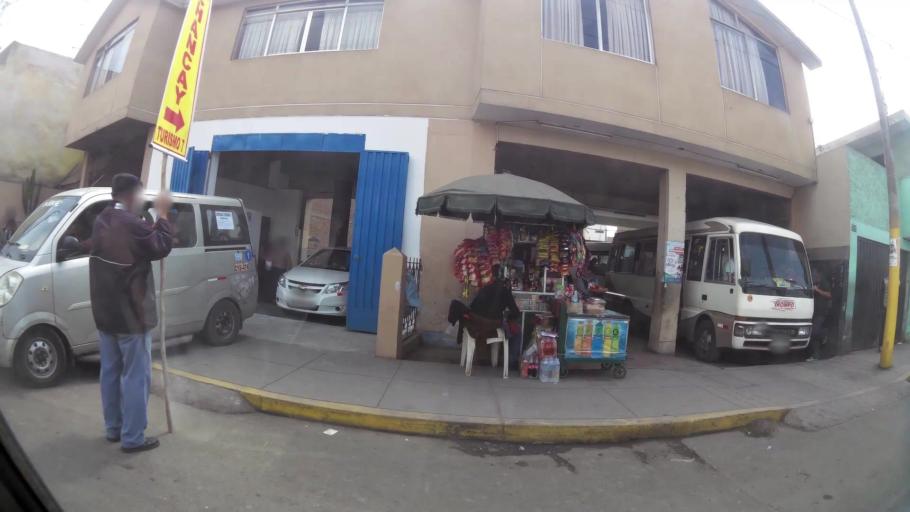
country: PE
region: Lima
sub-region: Provincia de Huaral
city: Huaral
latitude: -11.4964
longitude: -77.2103
